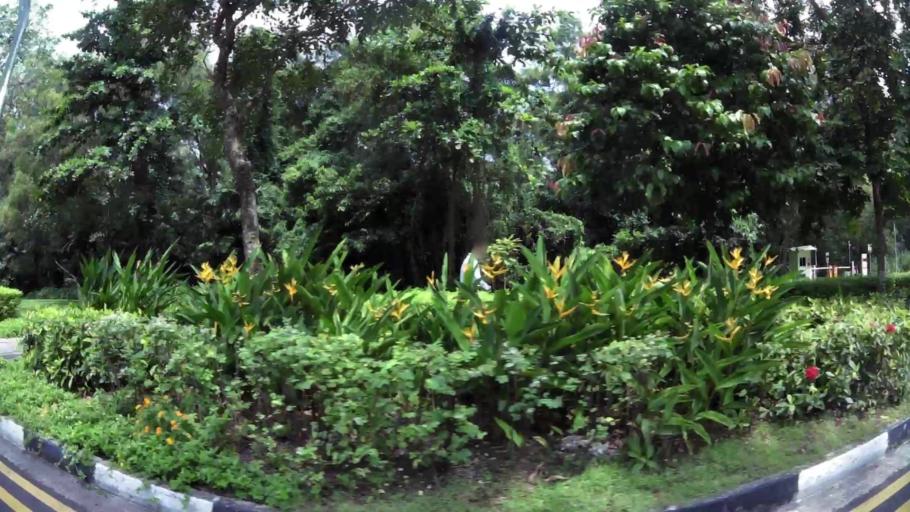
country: MY
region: Johor
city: Kampung Pasir Gudang Baru
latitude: 1.3750
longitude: 103.9514
